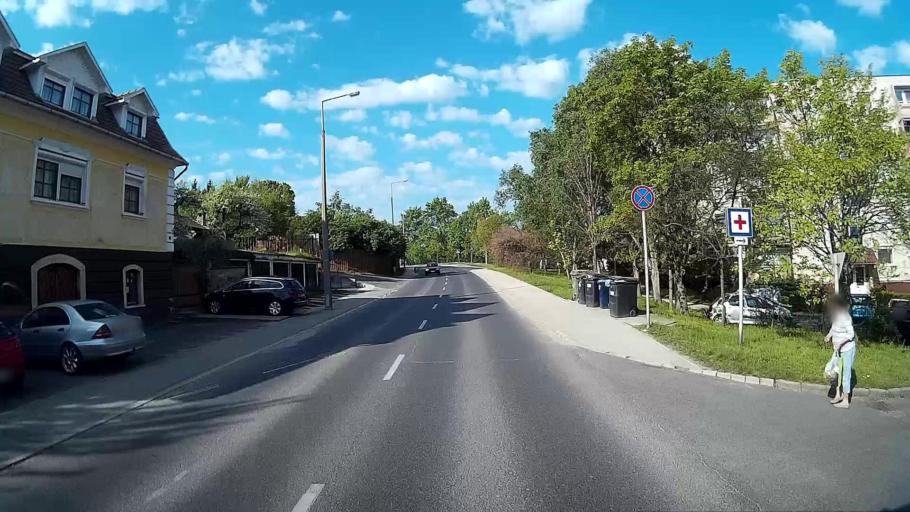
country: HU
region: Komarom-Esztergom
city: Esztergom
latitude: 47.8011
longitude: 18.7500
